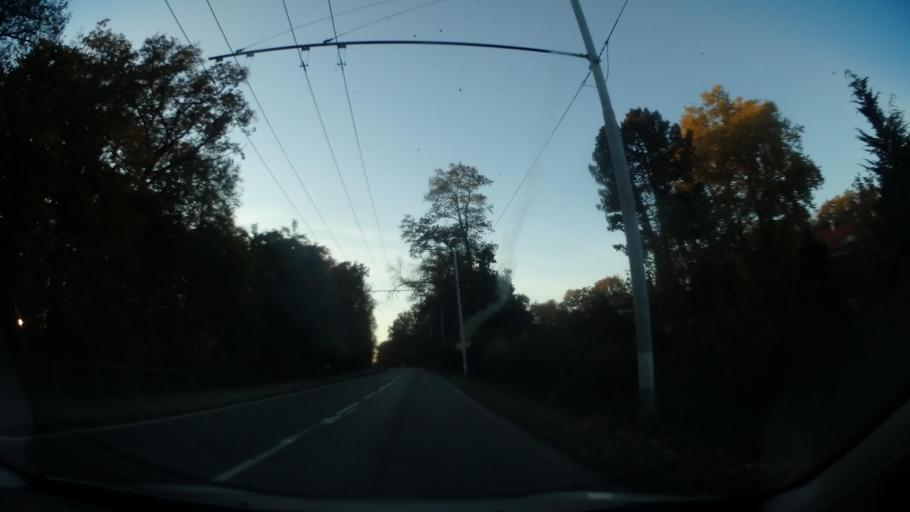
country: CZ
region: Pardubicky
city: Rybitvi
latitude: 50.0663
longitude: 15.7067
